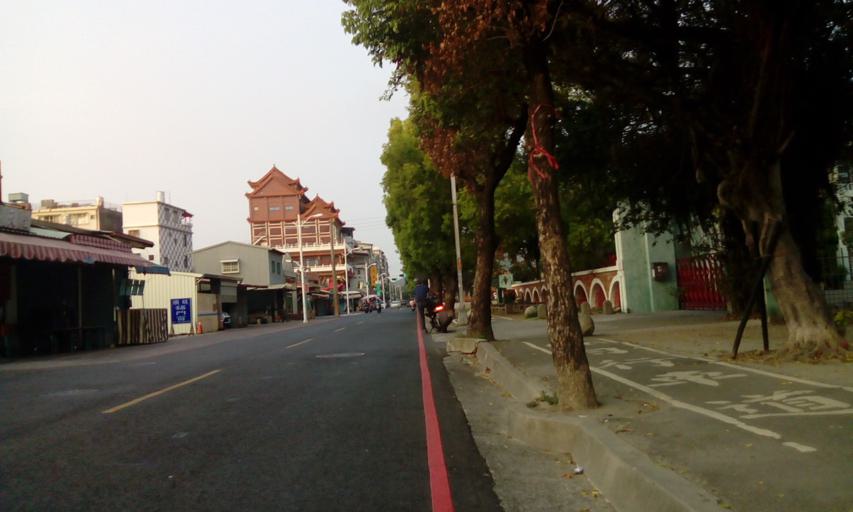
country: TW
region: Kaohsiung
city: Kaohsiung
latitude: 22.6842
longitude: 120.2943
